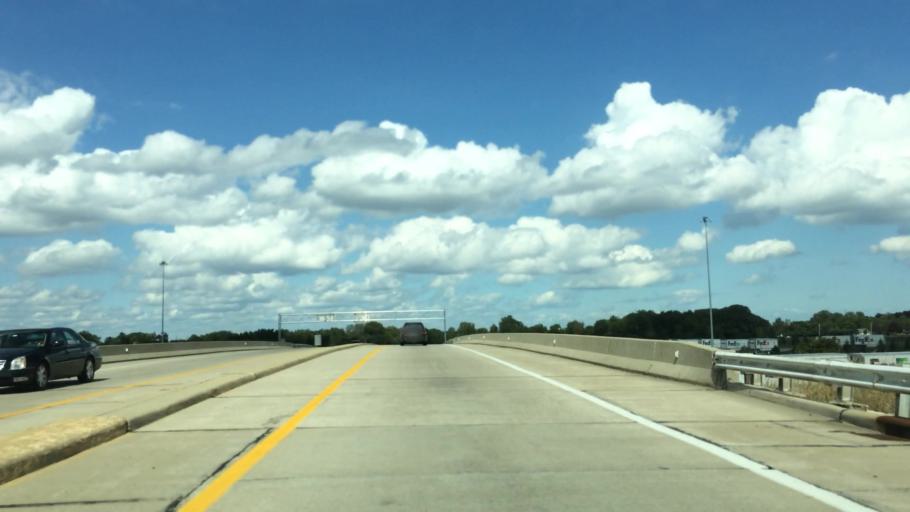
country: US
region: Ohio
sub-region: Wood County
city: Rossford
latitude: 41.5661
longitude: -83.5755
